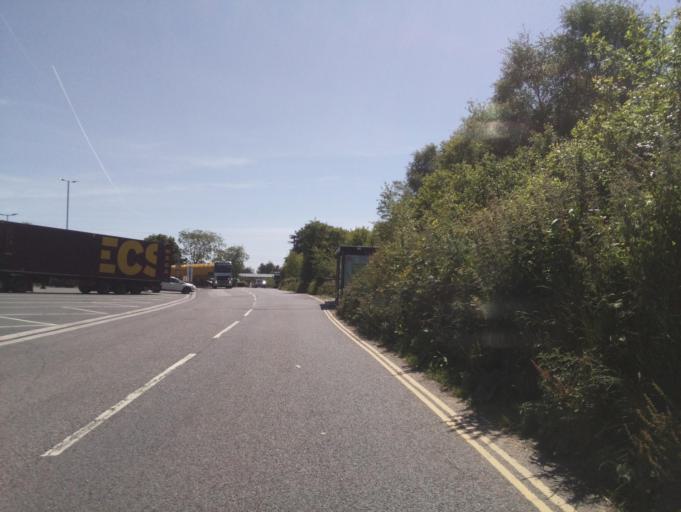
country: GB
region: England
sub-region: Devon
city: Chudleigh
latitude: 50.6420
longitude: -3.5626
